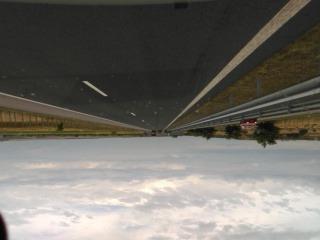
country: BG
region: Sliven
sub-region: Obshtina Sliven
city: Kermen
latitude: 42.5070
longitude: 26.3321
